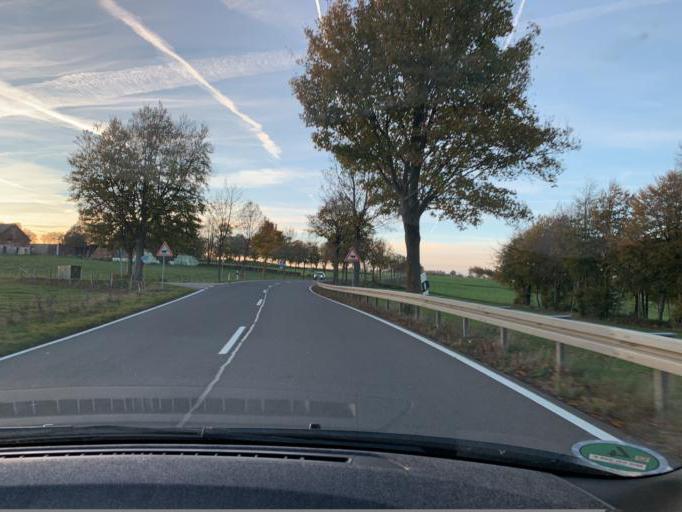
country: DE
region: North Rhine-Westphalia
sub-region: Regierungsbezirk Koln
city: Simmerath
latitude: 50.5945
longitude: 6.3553
